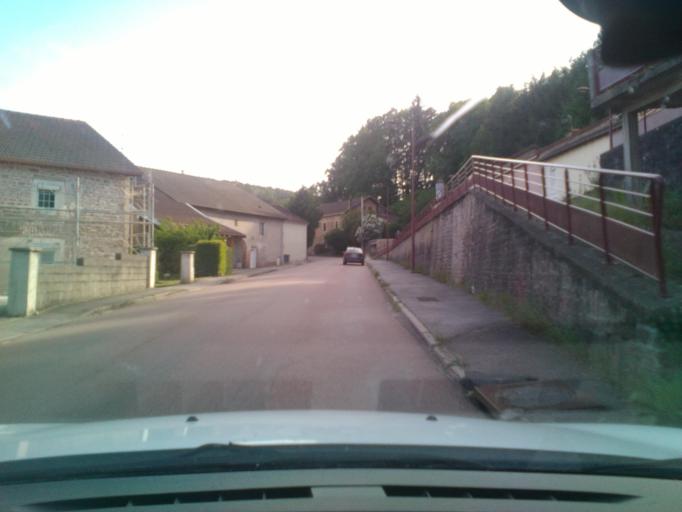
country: FR
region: Lorraine
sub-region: Departement des Vosges
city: Bruyeres
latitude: 48.2398
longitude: 6.7318
